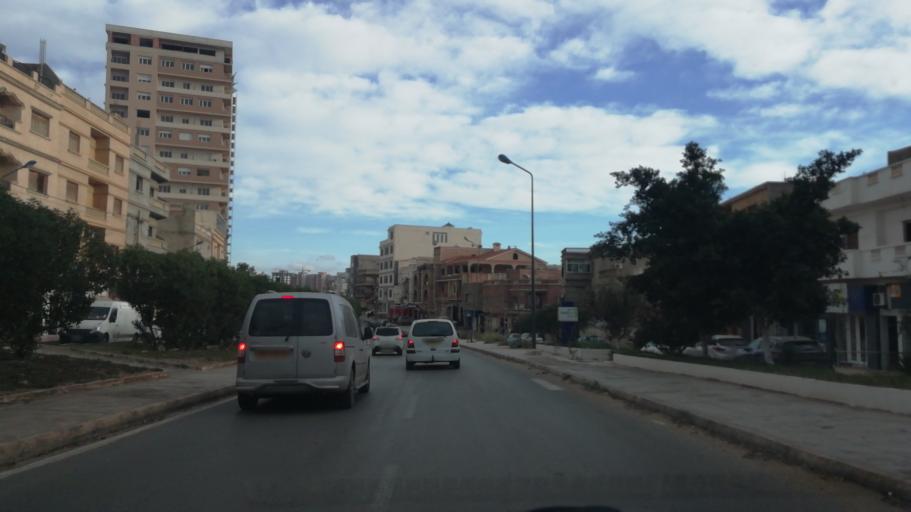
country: DZ
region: Oran
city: Bir el Djir
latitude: 35.7189
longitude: -0.5820
